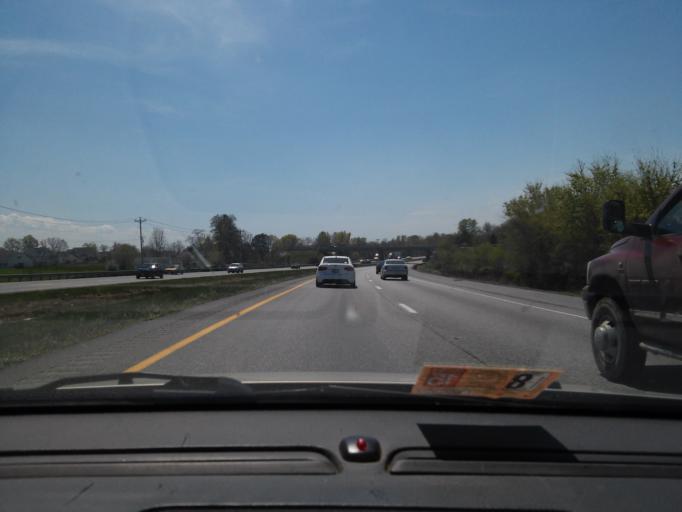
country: US
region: Pennsylvania
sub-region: Franklin County
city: Scotland
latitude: 39.9550
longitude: -77.5822
